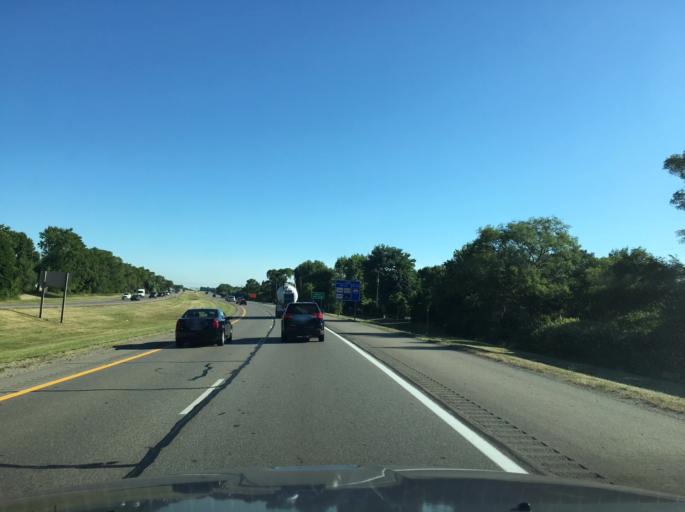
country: US
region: Michigan
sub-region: Macomb County
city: Utica
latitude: 42.6125
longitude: -83.0119
